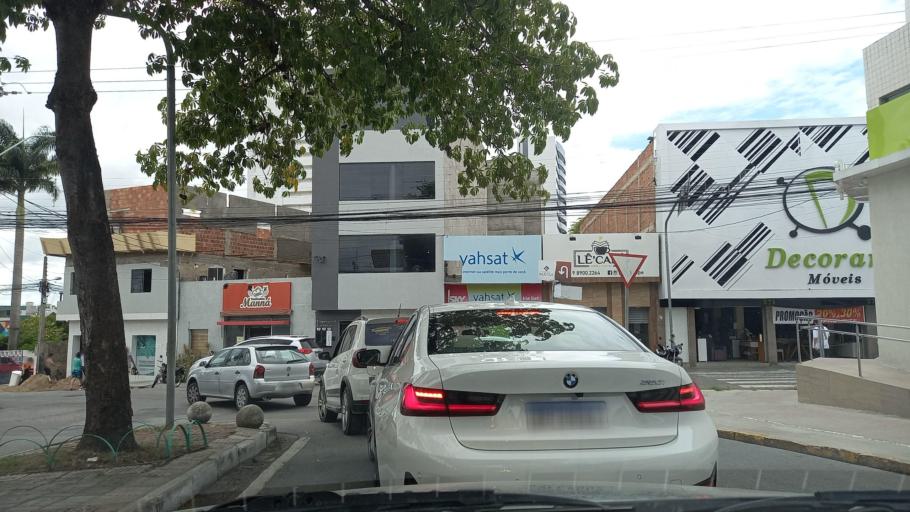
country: BR
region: Pernambuco
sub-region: Caruaru
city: Caruaru
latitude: -8.2800
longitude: -35.9691
